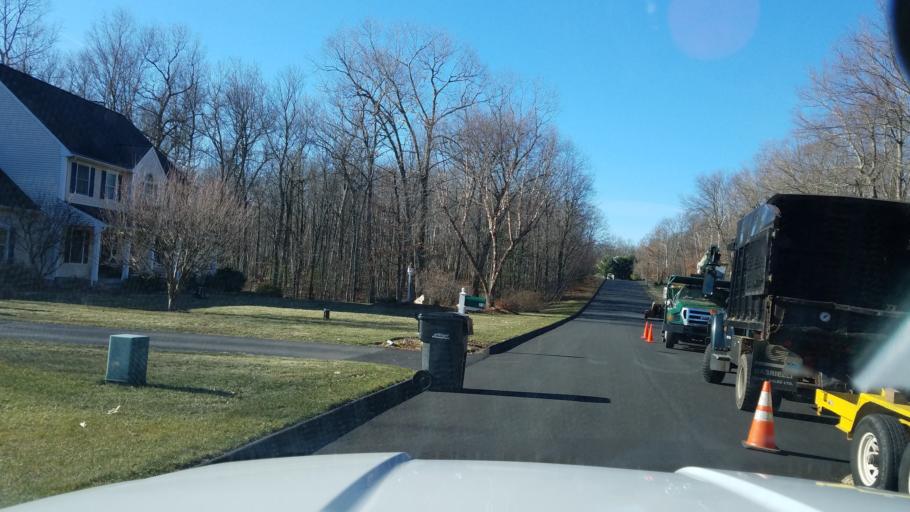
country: US
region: Connecticut
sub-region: Tolland County
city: Ellington
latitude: 41.9337
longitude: -72.4842
